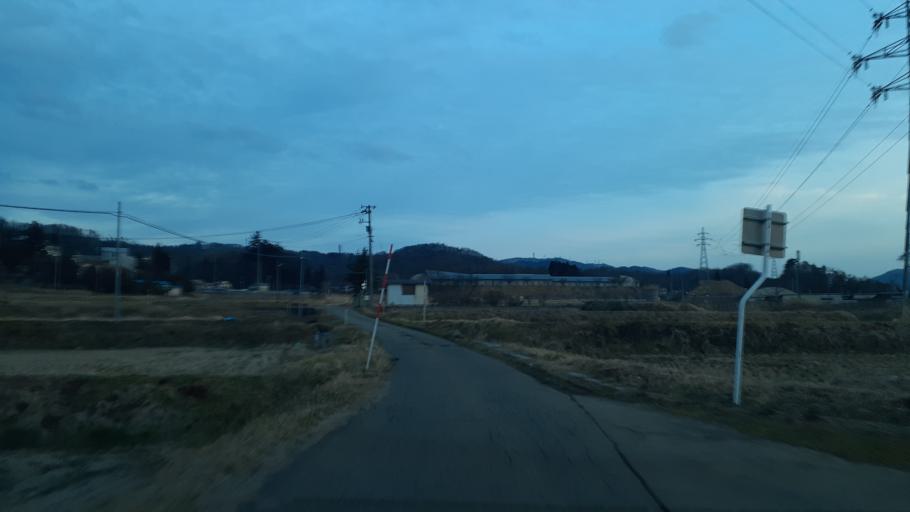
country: JP
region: Fukushima
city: Kitakata
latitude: 37.5262
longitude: 139.9518
